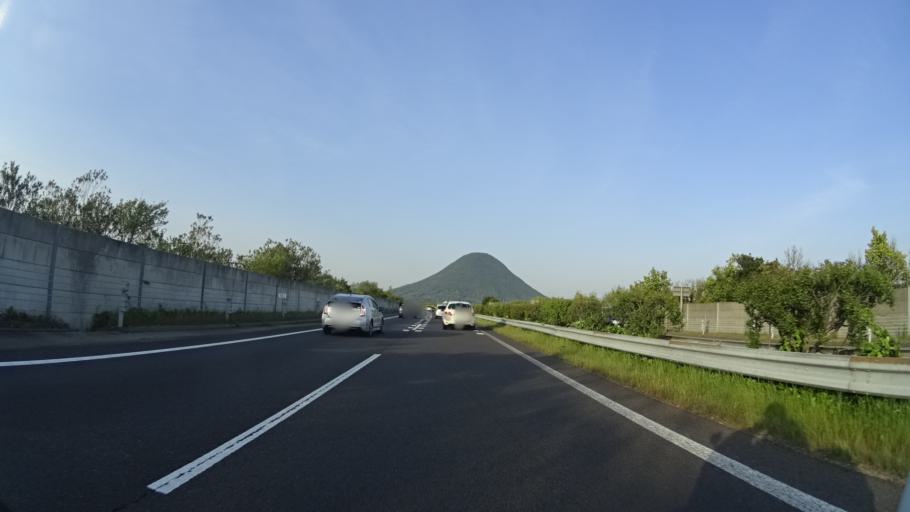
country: JP
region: Kagawa
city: Marugame
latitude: 34.2610
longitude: 133.8155
